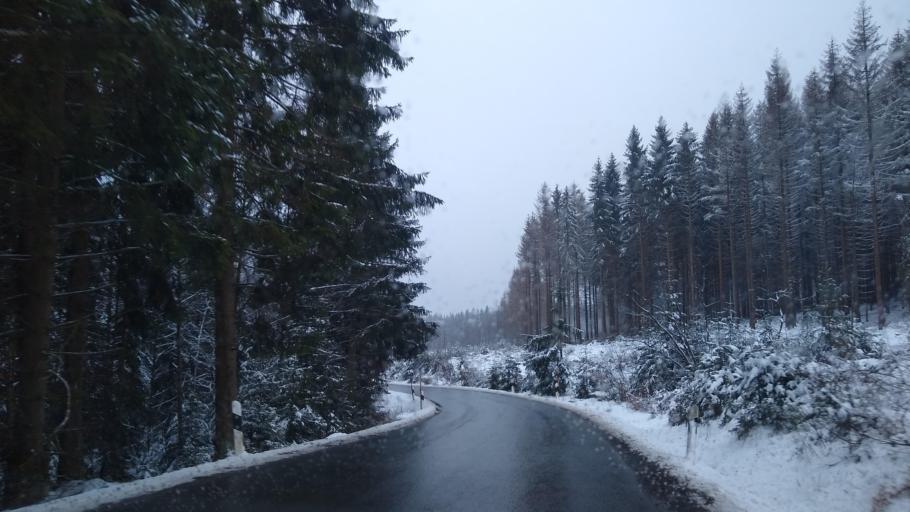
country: DE
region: Lower Saxony
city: Braunlage
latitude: 51.7482
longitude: 10.6307
